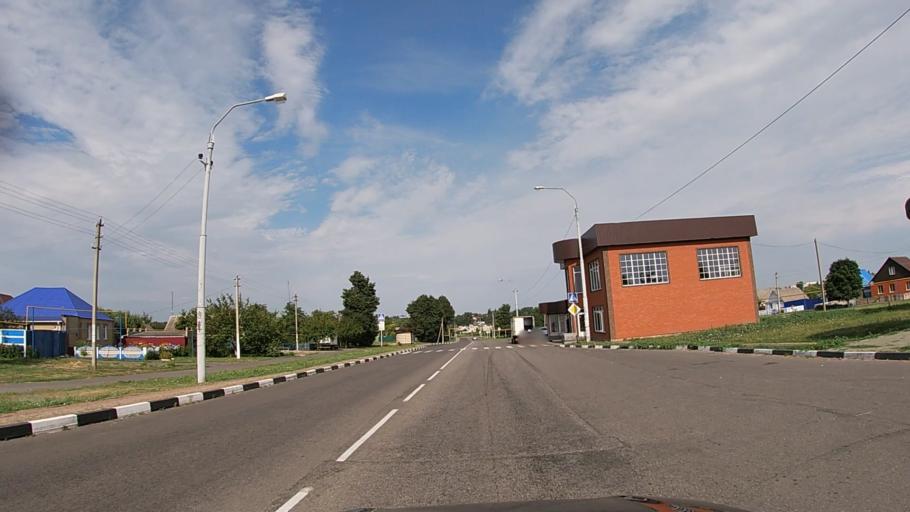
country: RU
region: Belgorod
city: Krasnaya Yaruga
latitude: 50.7997
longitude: 35.6761
